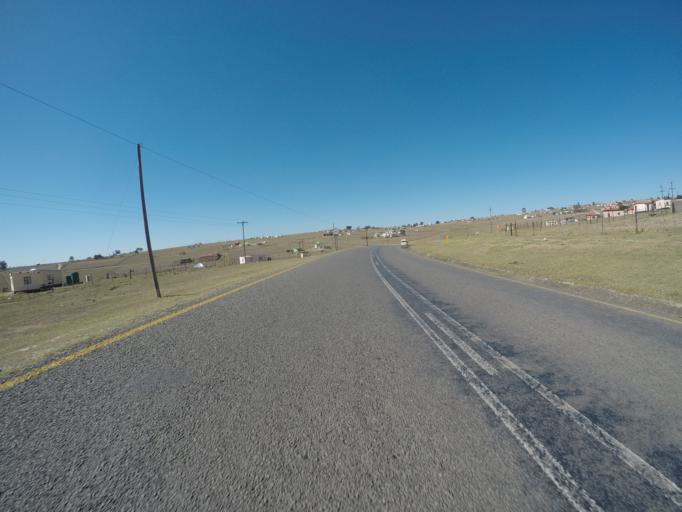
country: ZA
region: Eastern Cape
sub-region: OR Tambo District Municipality
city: Mthatha
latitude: -31.8796
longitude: 28.7559
